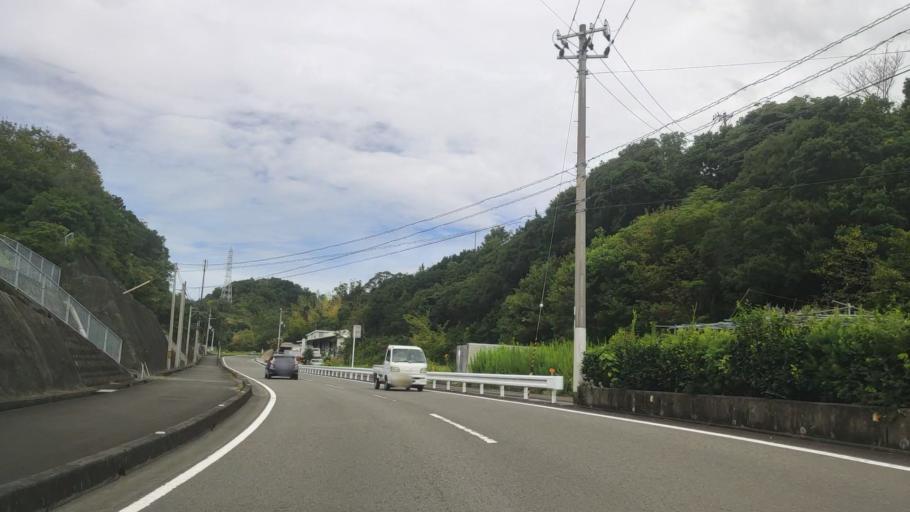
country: JP
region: Wakayama
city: Tanabe
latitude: 33.6828
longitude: 135.3889
